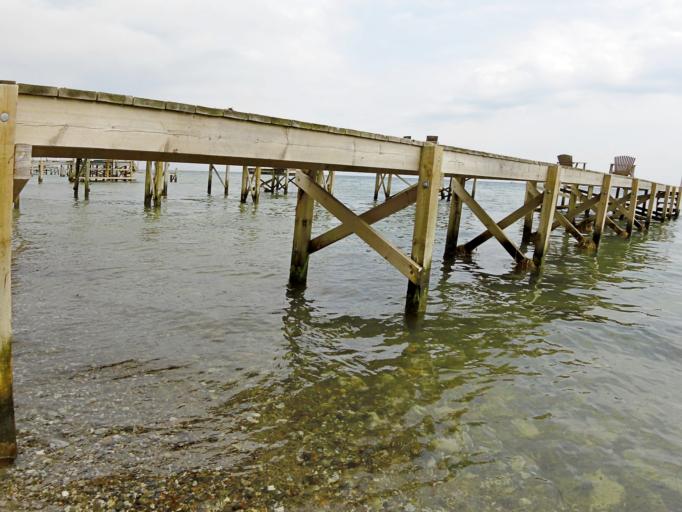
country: DK
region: Capital Region
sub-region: Gentofte Kommune
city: Charlottenlund
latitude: 55.7830
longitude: 12.5937
